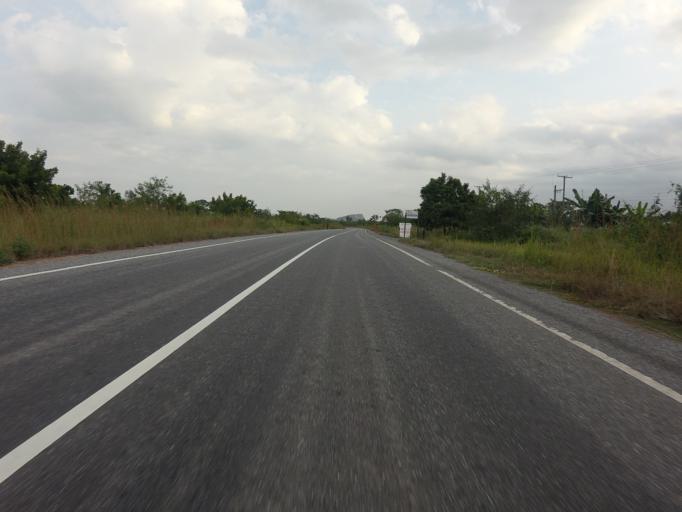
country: GH
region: Volta
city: Ho
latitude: 6.3496
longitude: 0.5378
